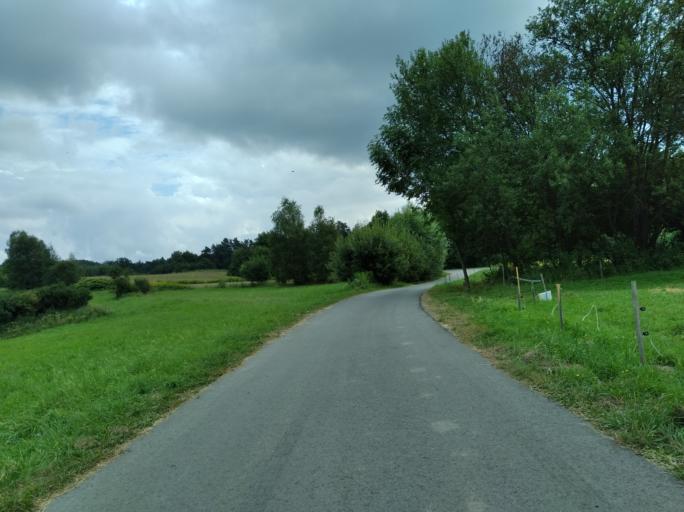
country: PL
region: Subcarpathian Voivodeship
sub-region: Powiat krosnienski
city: Odrzykon
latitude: 49.7759
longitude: 21.7290
